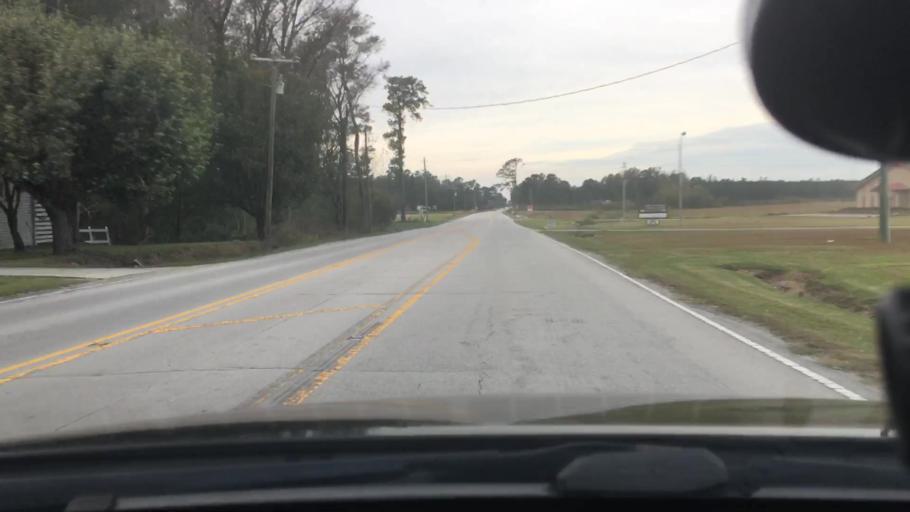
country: US
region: North Carolina
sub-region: Craven County
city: Vanceboro
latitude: 35.3511
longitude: -77.1880
